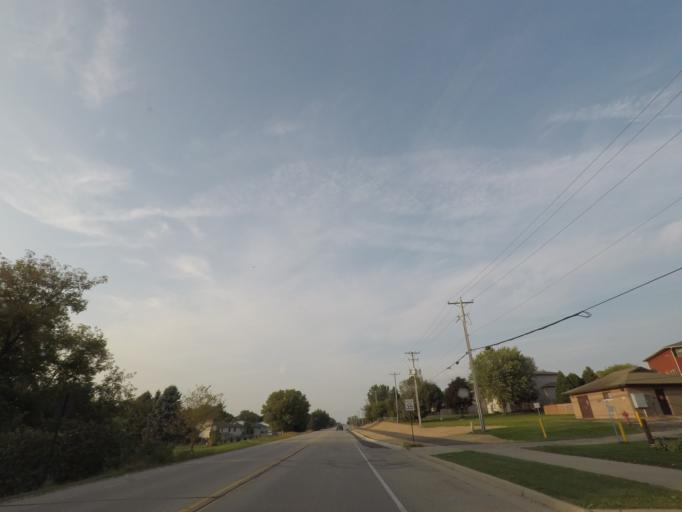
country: US
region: Wisconsin
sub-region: Dane County
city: Cottage Grove
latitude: 43.0907
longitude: -89.1996
